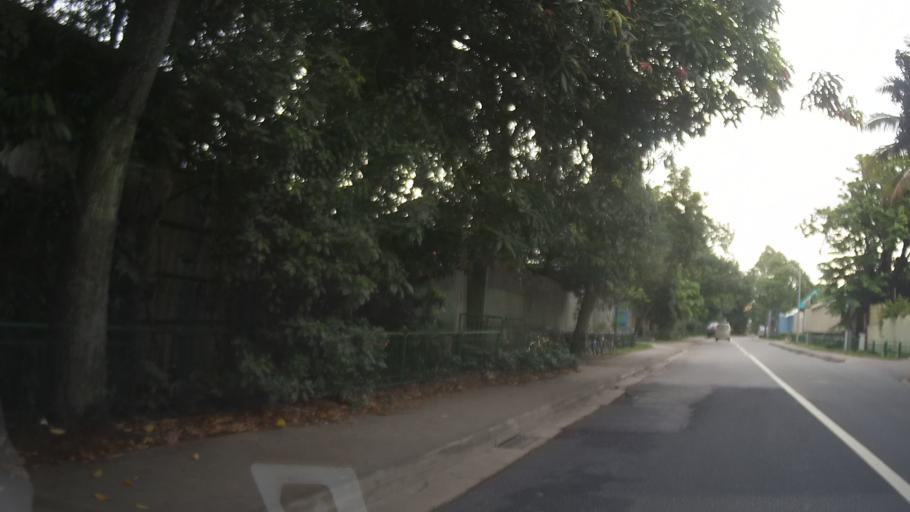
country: MY
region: Johor
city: Johor Bahru
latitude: 1.4212
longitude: 103.7485
